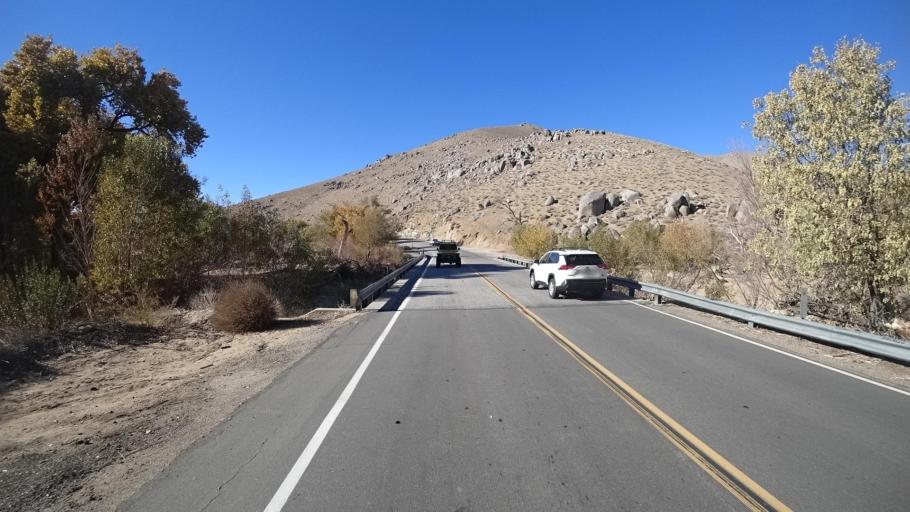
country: US
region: California
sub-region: Kern County
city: Weldon
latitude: 35.6723
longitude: -118.3271
